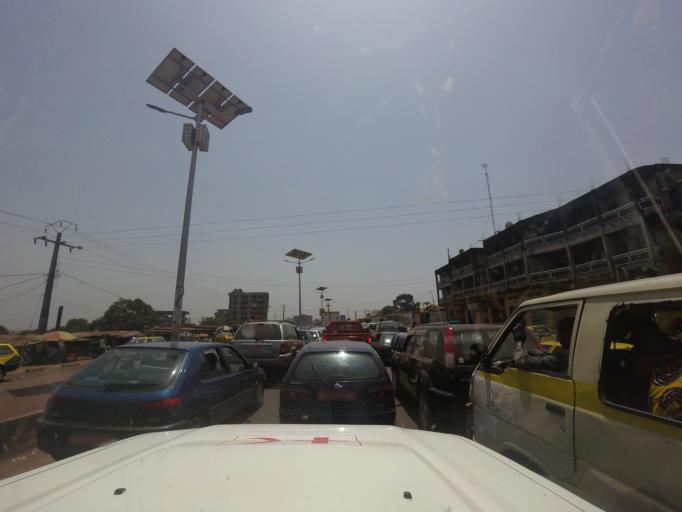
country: GN
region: Kindia
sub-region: Prefecture de Dubreka
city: Dubreka
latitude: 9.6457
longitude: -13.5615
